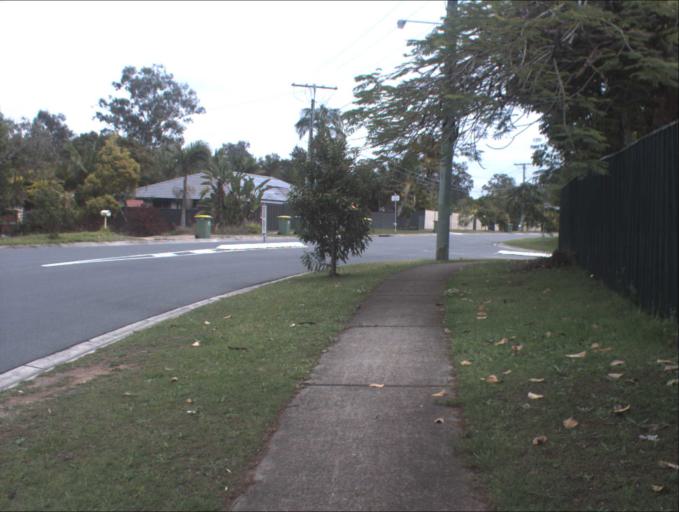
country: AU
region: Queensland
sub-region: Logan
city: Park Ridge South
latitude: -27.6906
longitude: 153.0212
